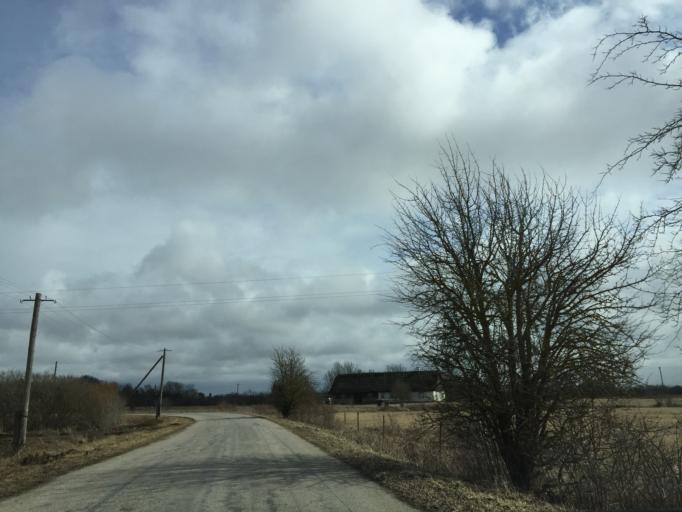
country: EE
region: Laeaene
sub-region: Lihula vald
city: Lihula
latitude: 58.7345
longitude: 23.8485
